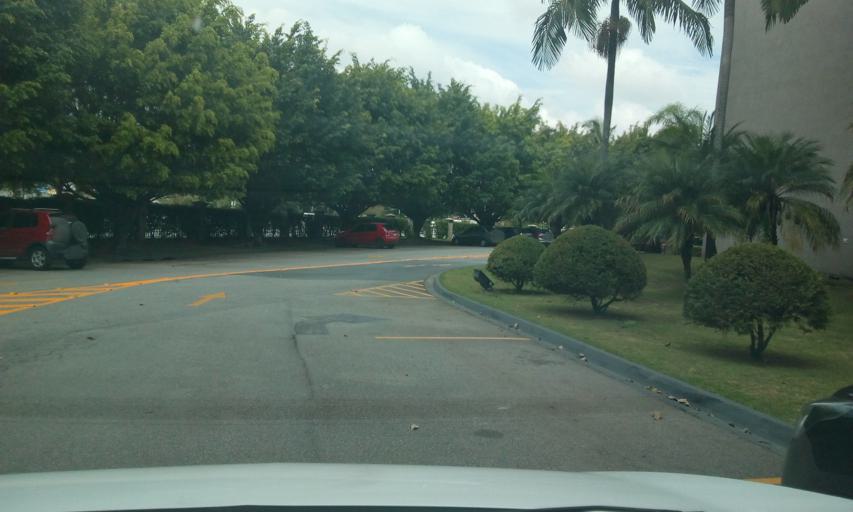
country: BR
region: Sao Paulo
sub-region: Guarulhos
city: Guarulhos
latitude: -23.4563
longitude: -46.4920
